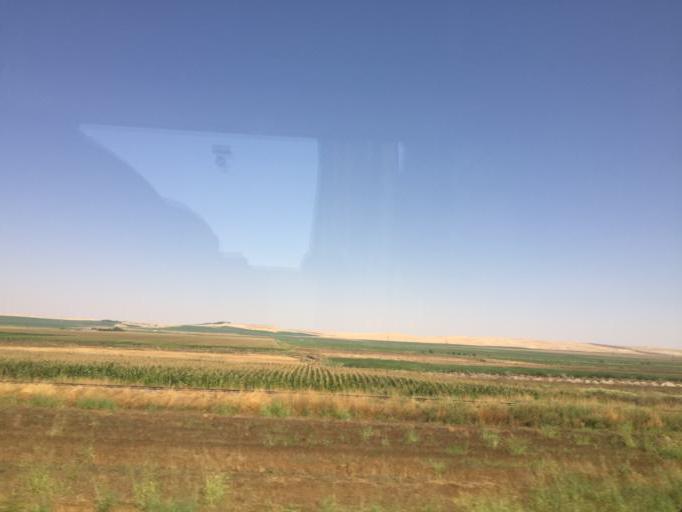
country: TR
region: Diyarbakir
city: Tepe
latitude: 37.8498
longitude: 40.7854
